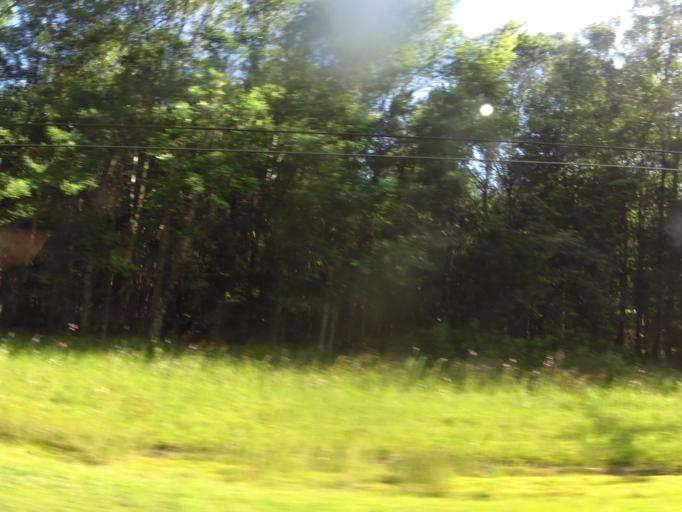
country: US
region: Florida
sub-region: Nassau County
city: Nassau Village-Ratliff
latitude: 30.4665
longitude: -81.8086
